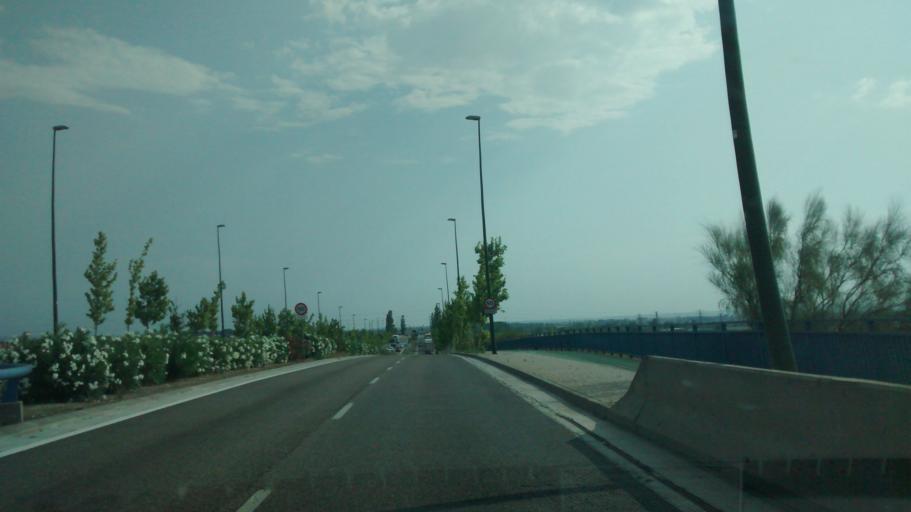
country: ES
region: Aragon
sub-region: Provincia de Zaragoza
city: Zaragoza
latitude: 41.6738
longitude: -0.8544
